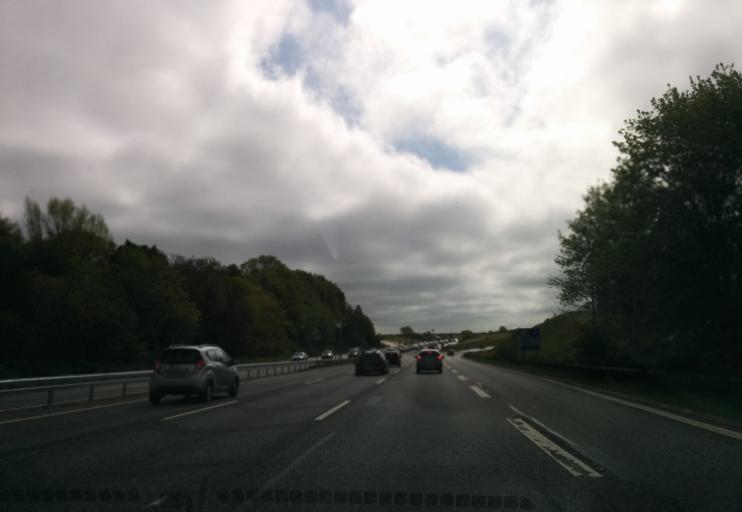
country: DK
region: South Denmark
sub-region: Middelfart Kommune
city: Strib
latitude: 55.5156
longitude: 9.7639
